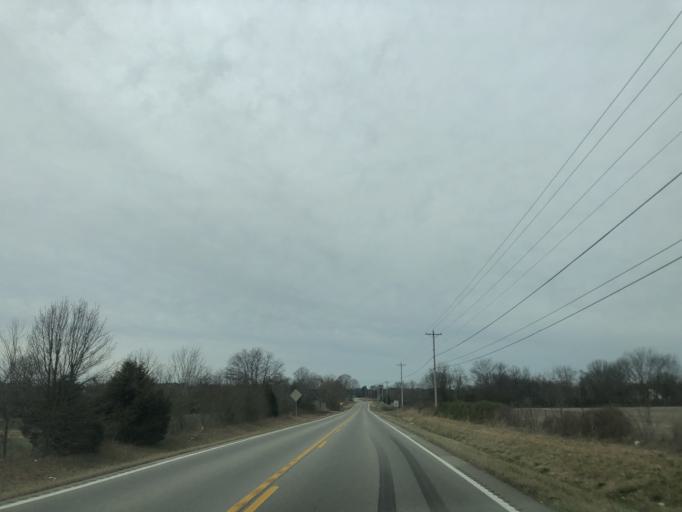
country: US
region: Tennessee
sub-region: Robertson County
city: Greenbrier
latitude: 36.4009
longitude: -86.8115
